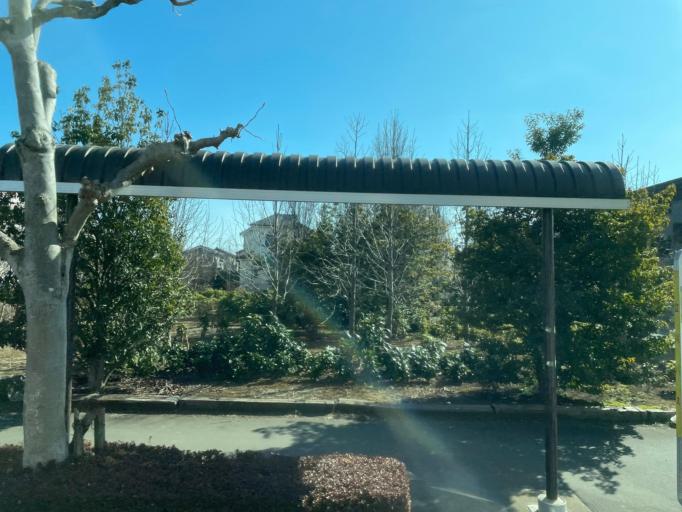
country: JP
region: Tokyo
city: Fussa
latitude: 35.7541
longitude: 139.3626
